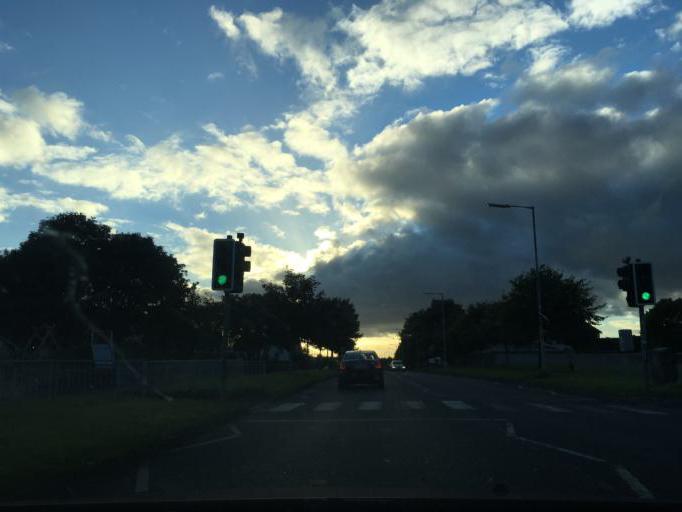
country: IE
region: Leinster
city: Oldbawn
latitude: 53.2768
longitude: -6.3639
